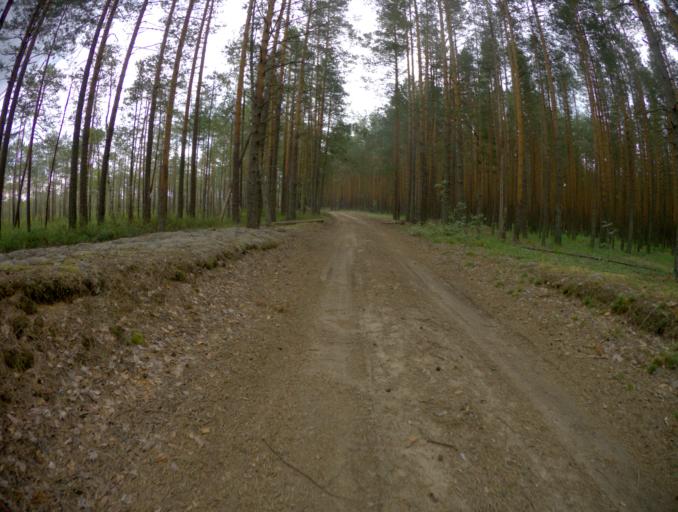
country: RU
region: Nizjnij Novgorod
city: Frolishchi
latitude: 56.3240
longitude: 42.7056
